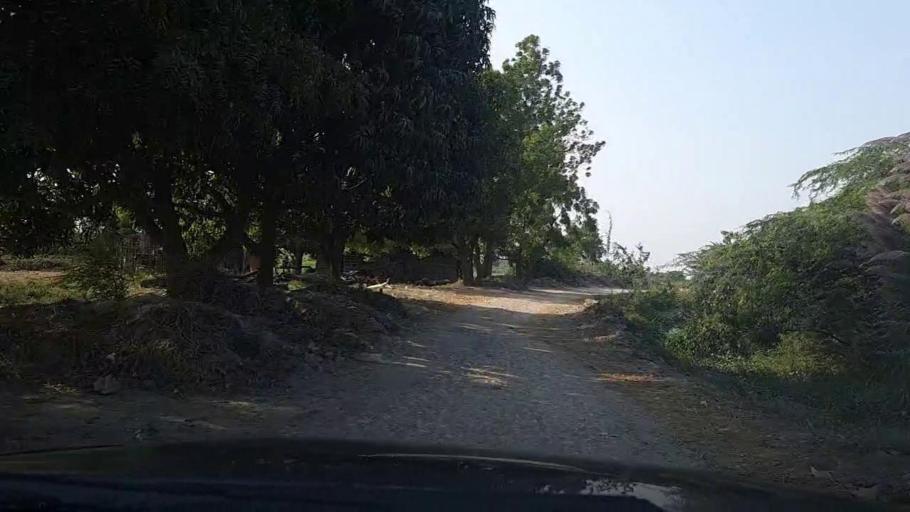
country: PK
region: Sindh
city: Mirpur Sakro
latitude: 24.6357
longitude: 67.7523
